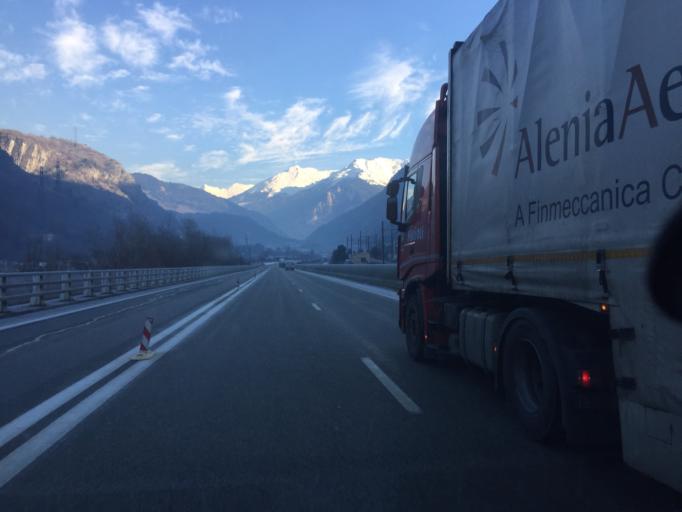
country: FR
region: Rhone-Alpes
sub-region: Departement de la Savoie
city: Modane
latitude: 45.2059
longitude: 6.5753
